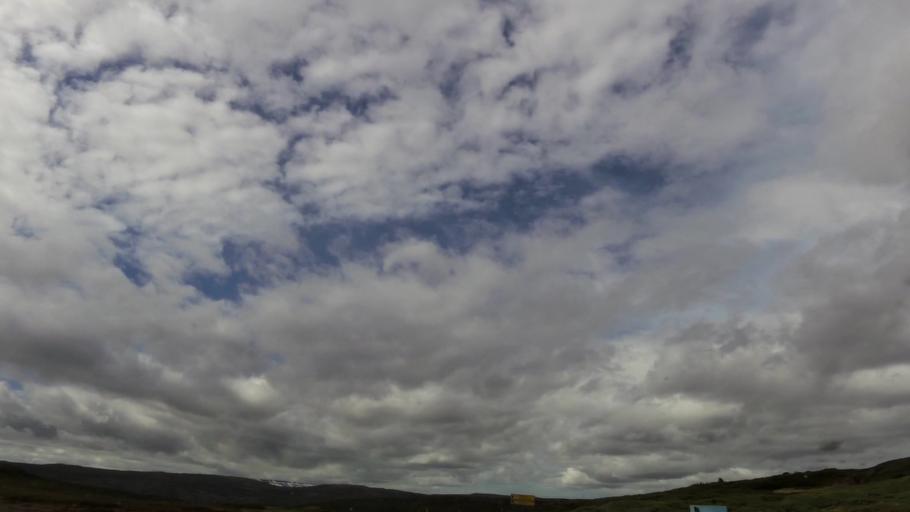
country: IS
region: West
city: Stykkisholmur
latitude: 65.5457
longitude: -22.0959
